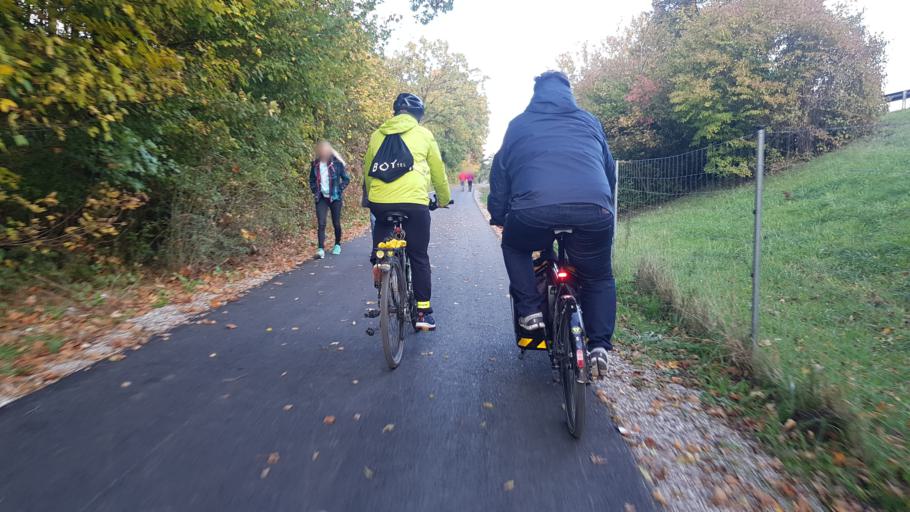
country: DE
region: Bavaria
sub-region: Upper Bavaria
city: Pasing
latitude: 48.1248
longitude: 11.4580
